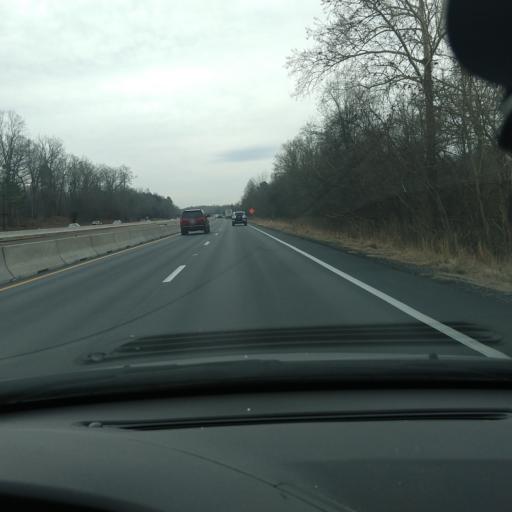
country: US
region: North Carolina
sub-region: Rowan County
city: China Grove
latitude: 35.5319
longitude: -80.5738
